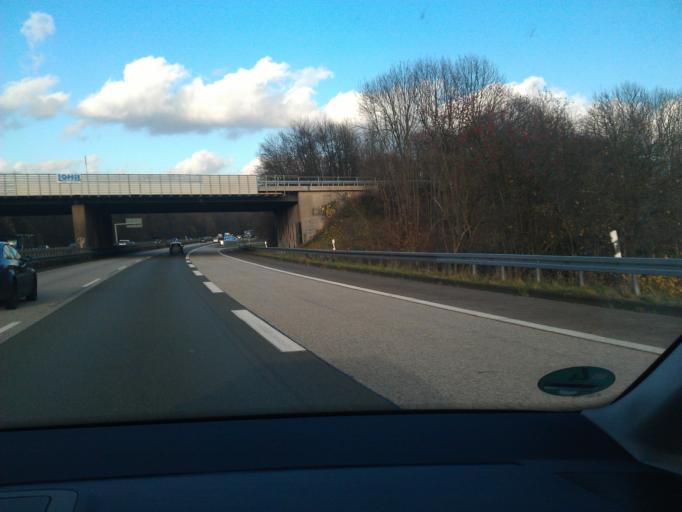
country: DE
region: North Rhine-Westphalia
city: Sprockhovel
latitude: 51.4135
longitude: 7.2616
